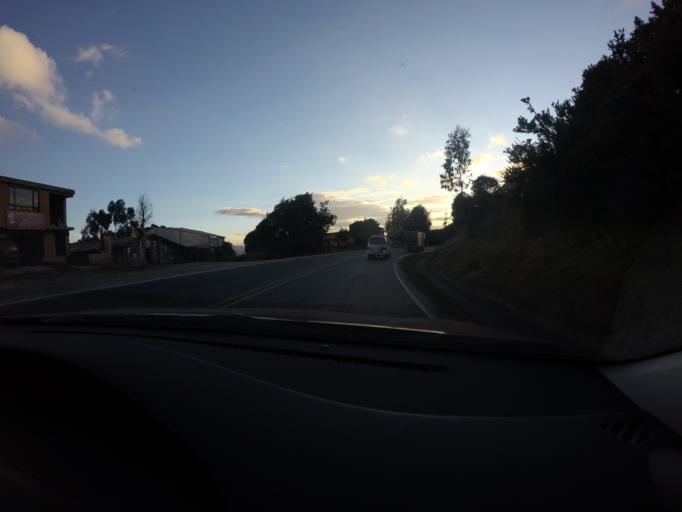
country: CO
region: Cundinamarca
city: Sutatausa
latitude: 5.1627
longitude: -73.8930
